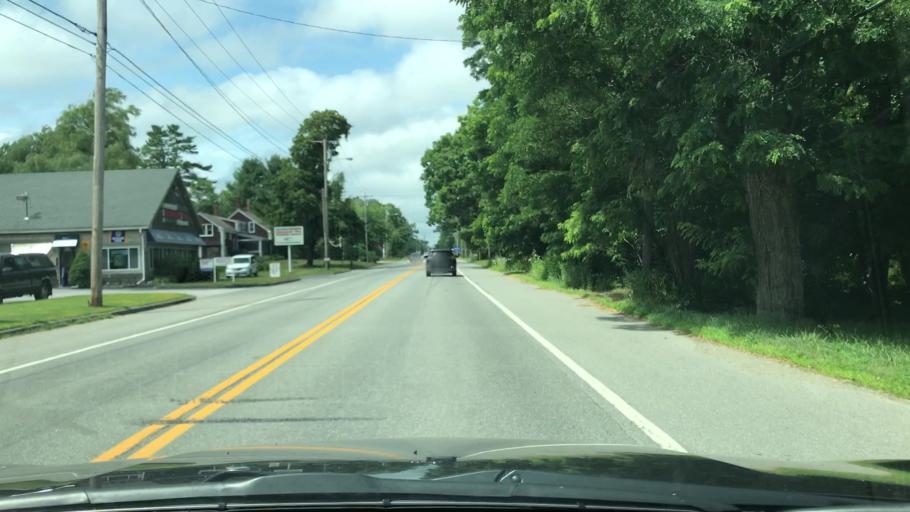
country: US
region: Maine
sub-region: Waldo County
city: Belfast
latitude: 44.4036
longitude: -68.9898
